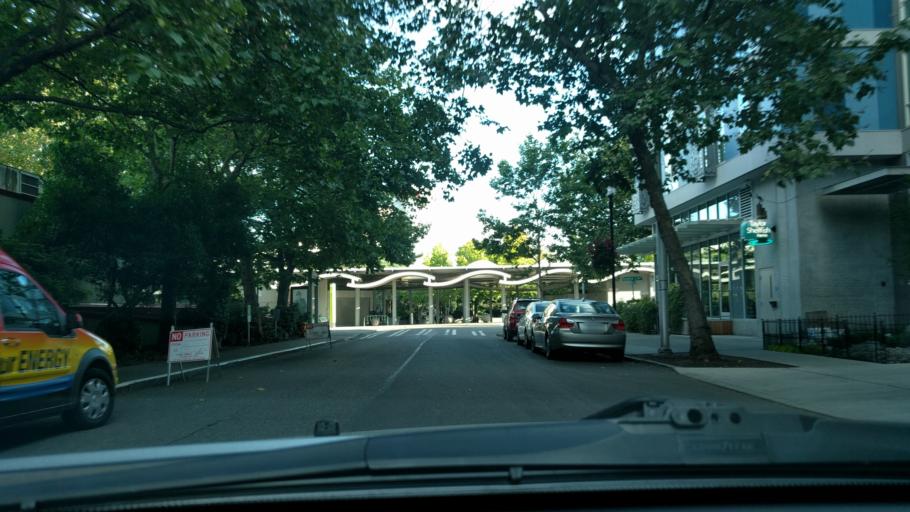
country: US
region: Washington
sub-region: King County
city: Seattle
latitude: 47.6237
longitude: -122.3542
